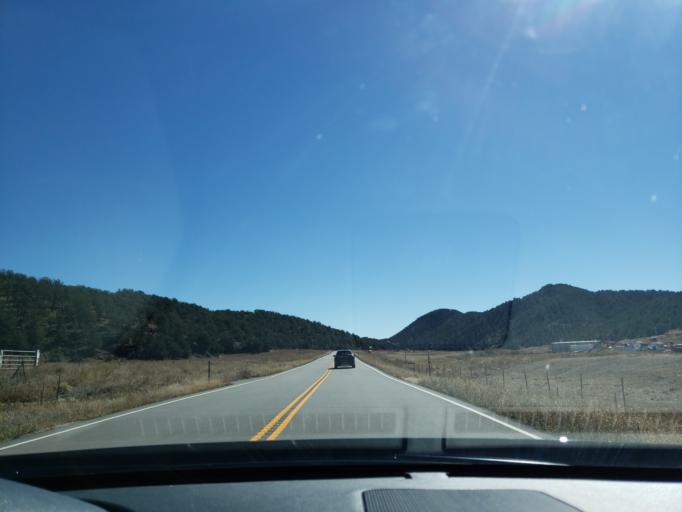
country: US
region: Colorado
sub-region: Fremont County
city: Canon City
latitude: 38.6305
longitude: -105.4613
